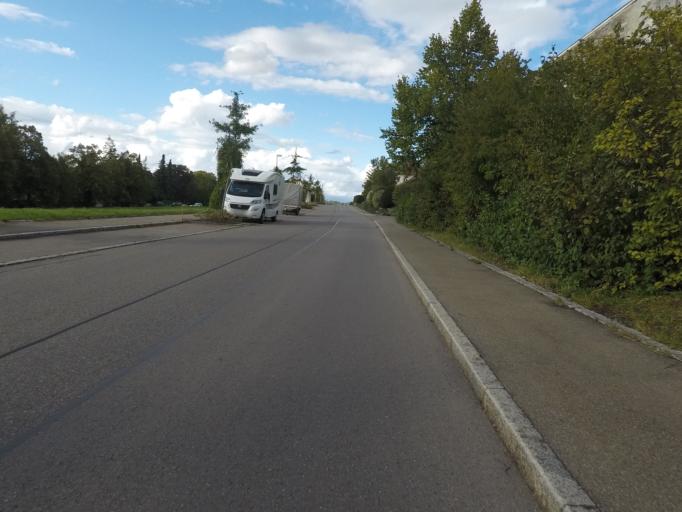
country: DE
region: Baden-Wuerttemberg
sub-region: Tuebingen Region
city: Pfullingen
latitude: 48.4661
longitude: 9.2316
